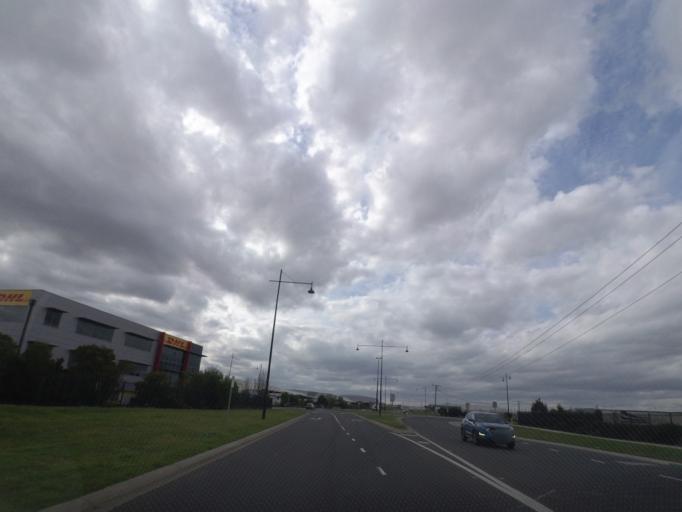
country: AU
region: Victoria
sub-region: Hume
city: Tullamarine
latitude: -37.6943
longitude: 144.8562
